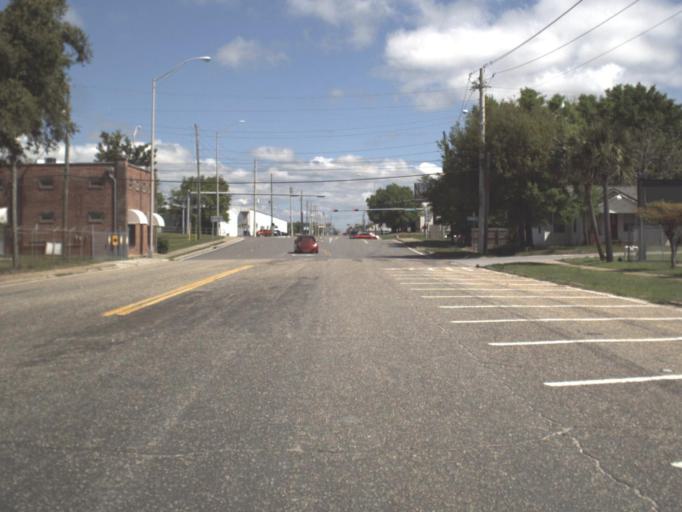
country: US
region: Florida
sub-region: Escambia County
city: Pensacola
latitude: 30.4022
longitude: -87.2422
